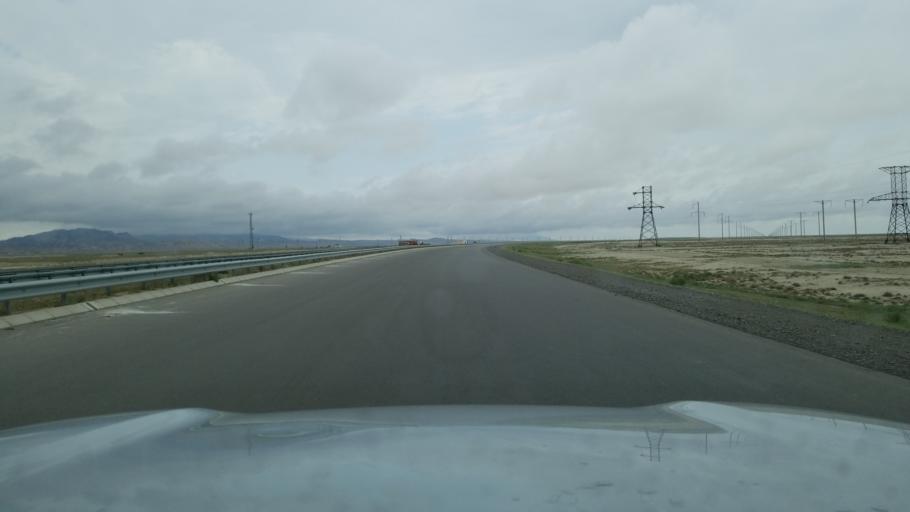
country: TM
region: Balkan
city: Serdar
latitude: 39.1042
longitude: 55.9391
